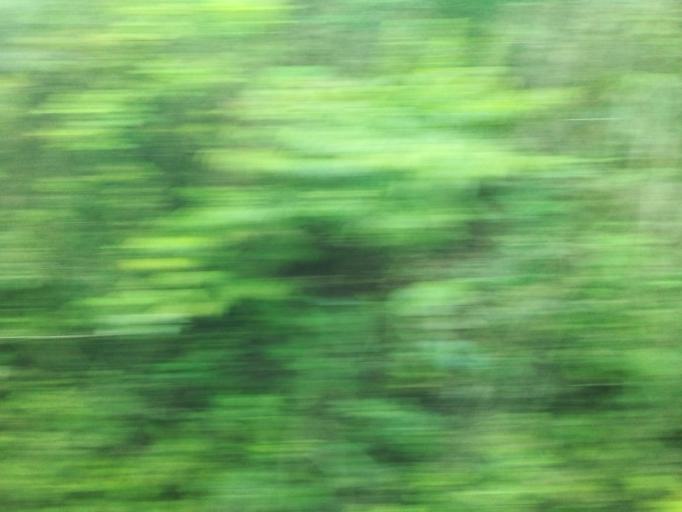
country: BR
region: Minas Gerais
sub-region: Nova Era
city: Nova Era
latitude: -19.7751
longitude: -43.0722
